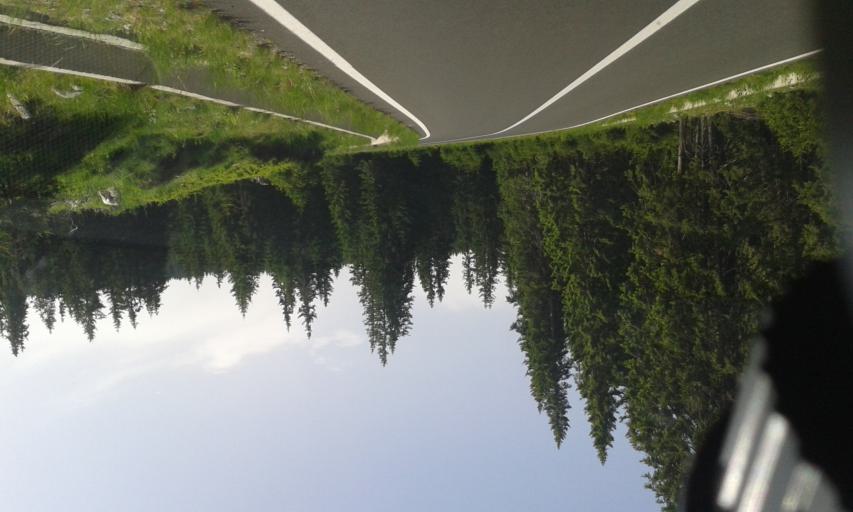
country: RO
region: Hunedoara
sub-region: Oras Petrila
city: Petrila
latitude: 45.4849
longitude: 23.6397
